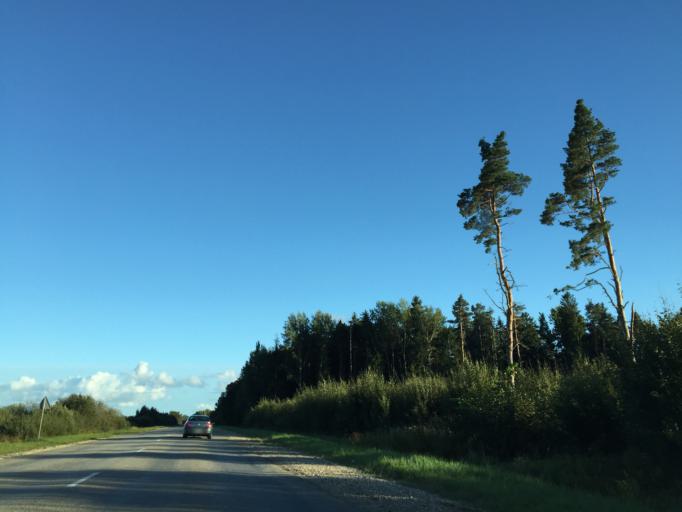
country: LV
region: Kuldigas Rajons
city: Kuldiga
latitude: 56.9522
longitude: 22.0111
